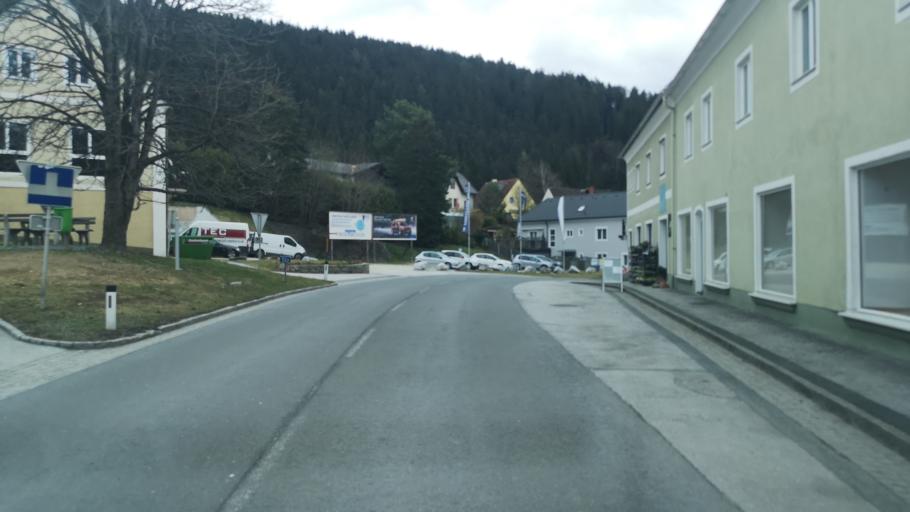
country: AT
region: Styria
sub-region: Politischer Bezirk Weiz
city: Birkfeld
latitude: 47.3570
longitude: 15.6984
